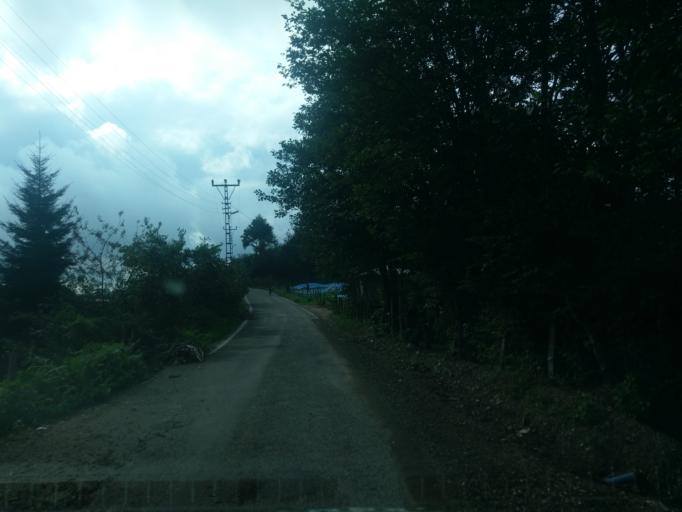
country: TR
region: Ordu
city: Camas
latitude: 40.8904
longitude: 37.6172
